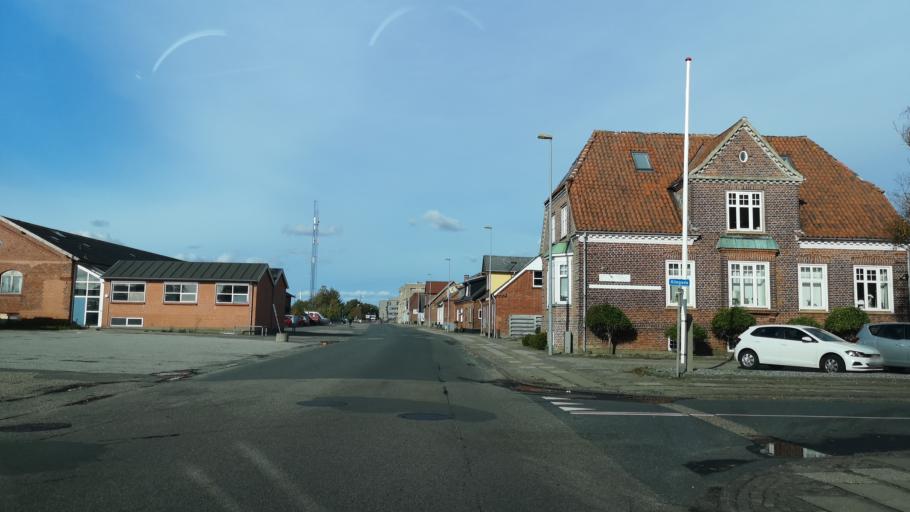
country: DK
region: Central Jutland
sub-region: Holstebro Kommune
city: Holstebro
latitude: 56.3661
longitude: 8.6215
